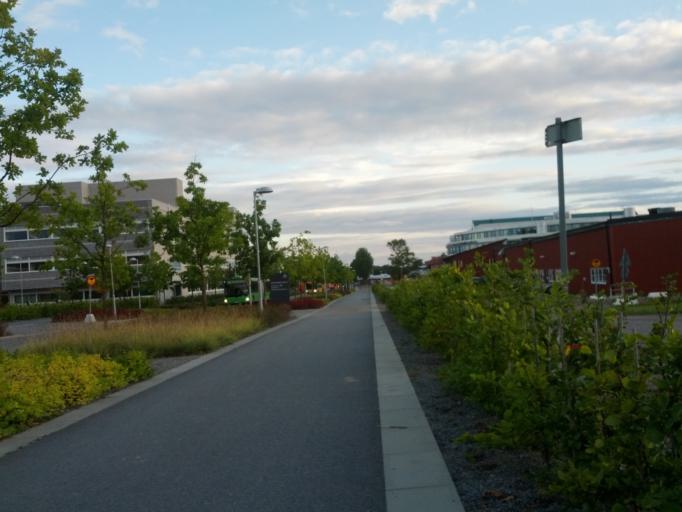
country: SE
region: Uppsala
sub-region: Uppsala Kommun
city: Saevja
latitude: 59.8171
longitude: 17.6590
